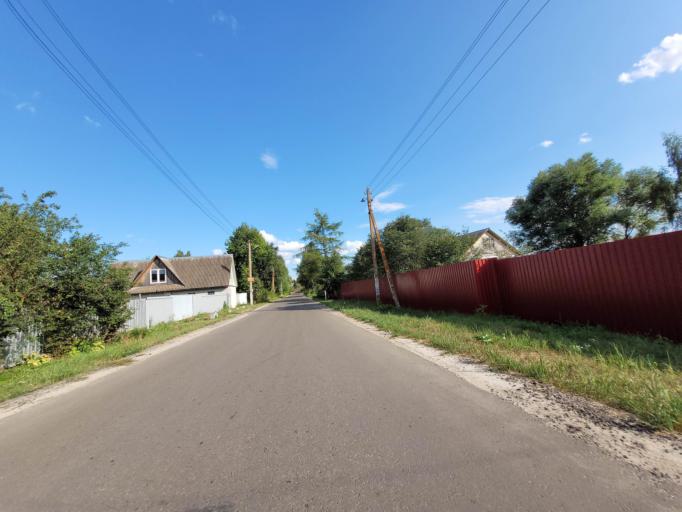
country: RU
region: Moskovskaya
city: Konobeyevo
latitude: 55.4076
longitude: 38.7023
